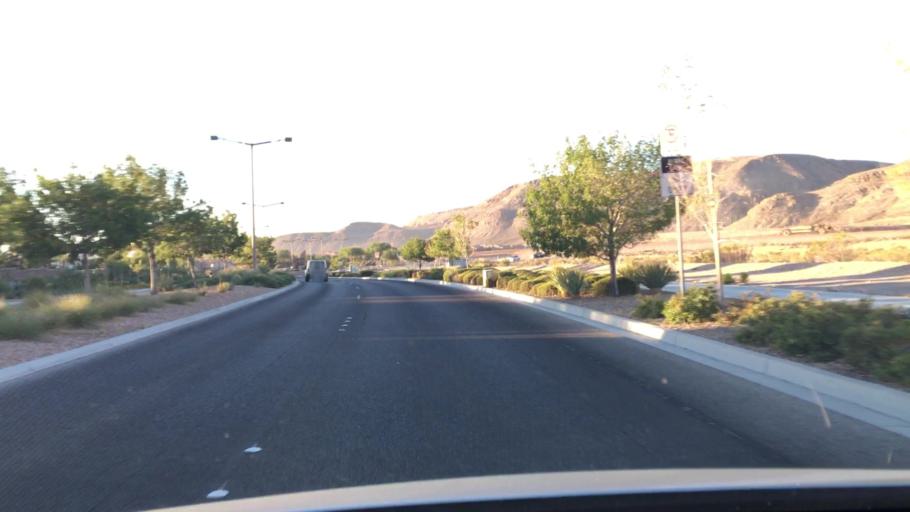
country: US
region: Nevada
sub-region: Clark County
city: Summerlin South
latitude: 36.0964
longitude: -115.3253
